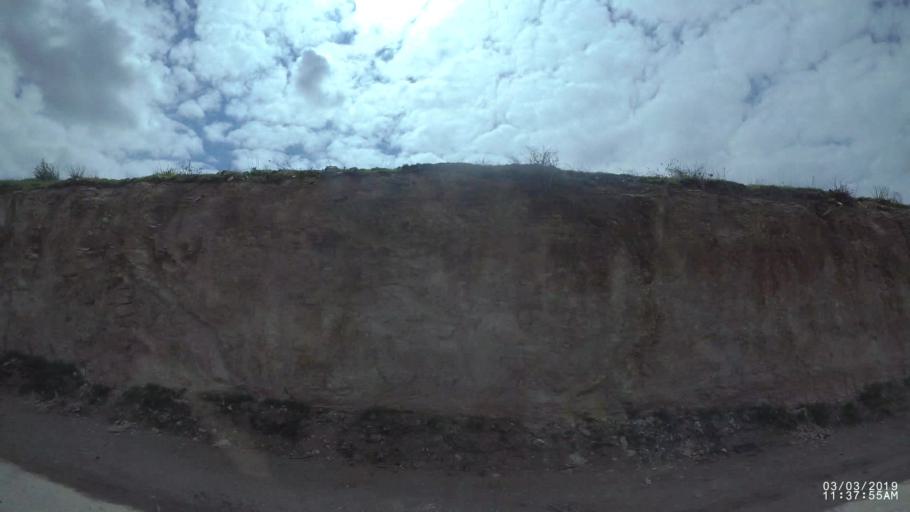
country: JO
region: Amman
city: Amman
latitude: 32.0021
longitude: 35.9163
